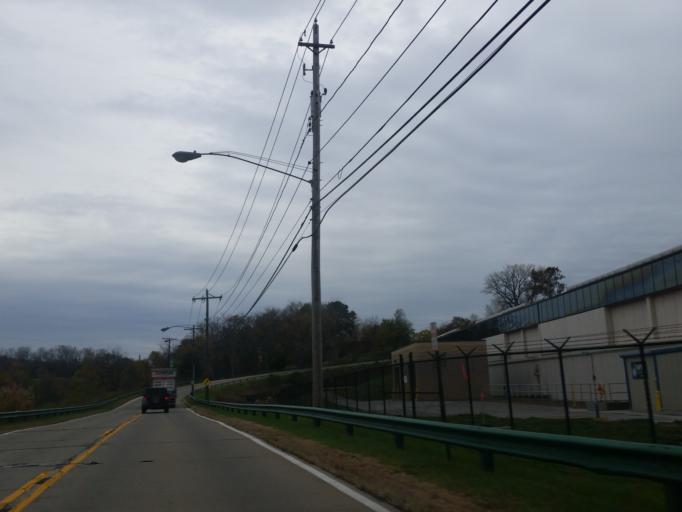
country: US
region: Ohio
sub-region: Cuyahoga County
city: Newburgh Heights
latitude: 41.4220
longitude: -81.6528
